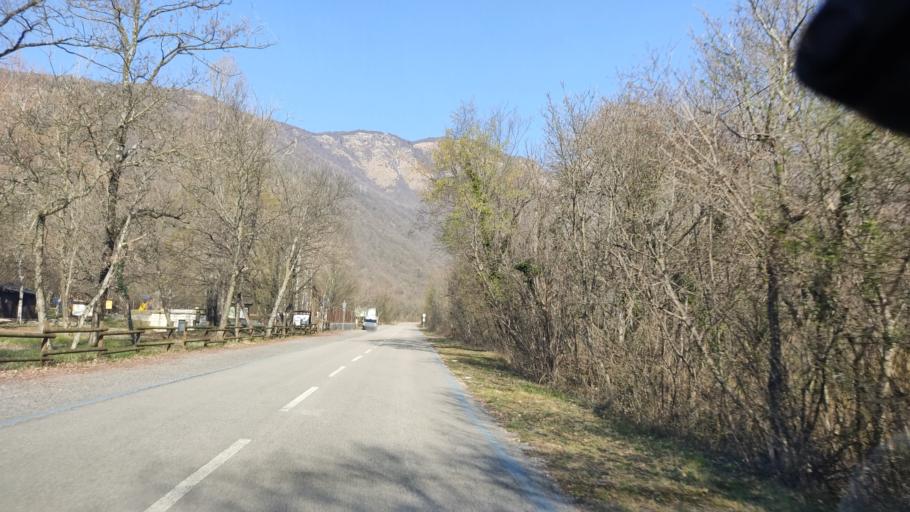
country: IT
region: Friuli Venezia Giulia
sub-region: Provincia di Pordenone
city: Budoia
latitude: 46.0589
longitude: 12.5225
